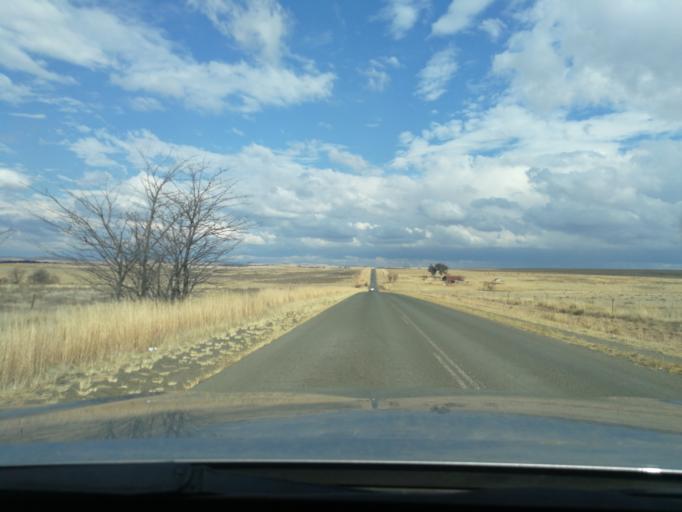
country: ZA
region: Orange Free State
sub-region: Fezile Dabi District Municipality
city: Frankfort
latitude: -27.4433
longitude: 28.5147
